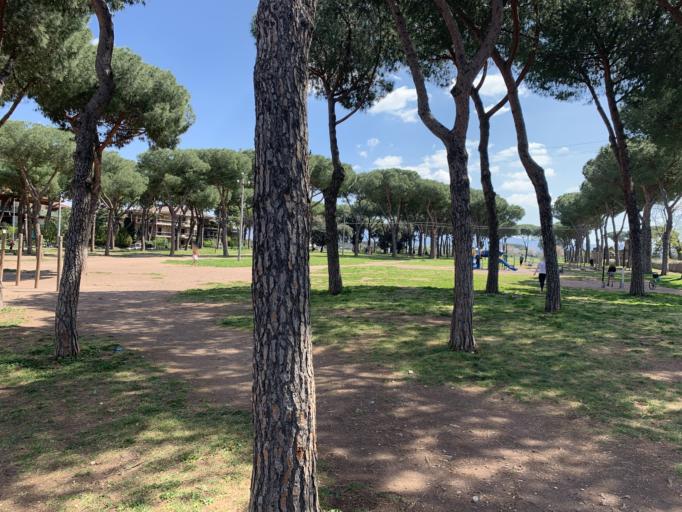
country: IT
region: Latium
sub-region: Citta metropolitana di Roma Capitale
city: Rome
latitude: 41.8488
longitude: 12.5610
